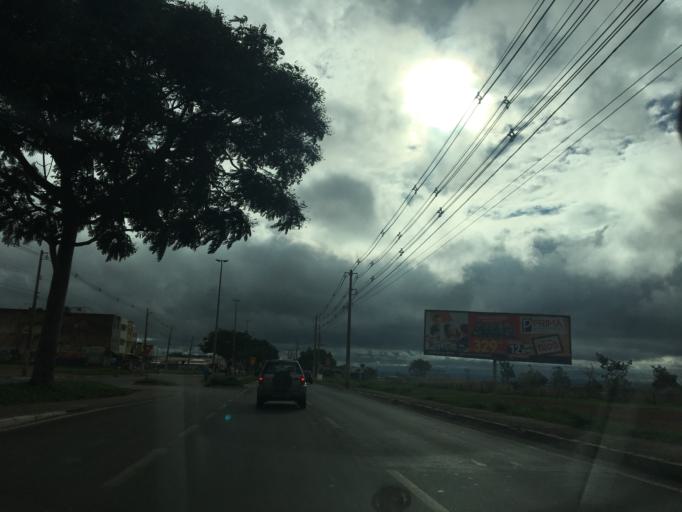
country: BR
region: Goias
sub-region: Luziania
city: Luziania
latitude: -16.0183
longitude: -48.0199
